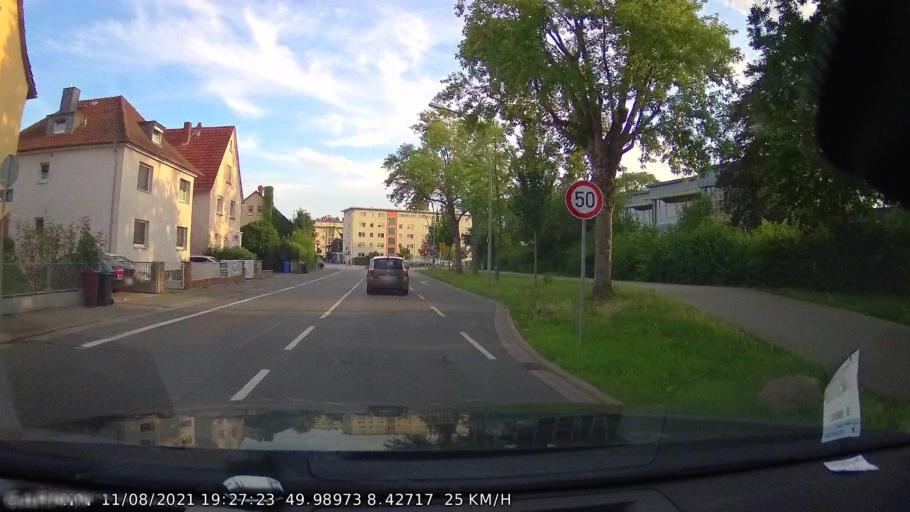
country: DE
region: Hesse
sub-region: Regierungsbezirk Darmstadt
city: Russelsheim
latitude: 49.9898
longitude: 8.4271
